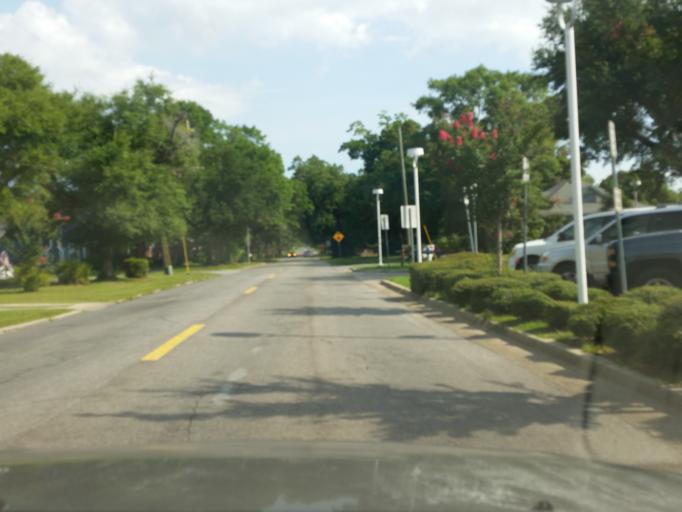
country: US
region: Florida
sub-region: Escambia County
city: Pensacola
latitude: 30.4290
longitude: -87.2038
